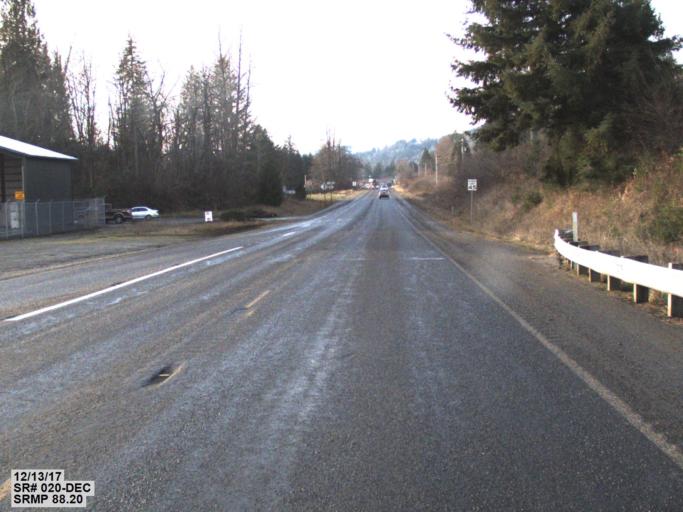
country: US
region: Washington
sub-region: Snohomish County
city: Darrington
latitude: 48.5370
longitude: -121.7663
